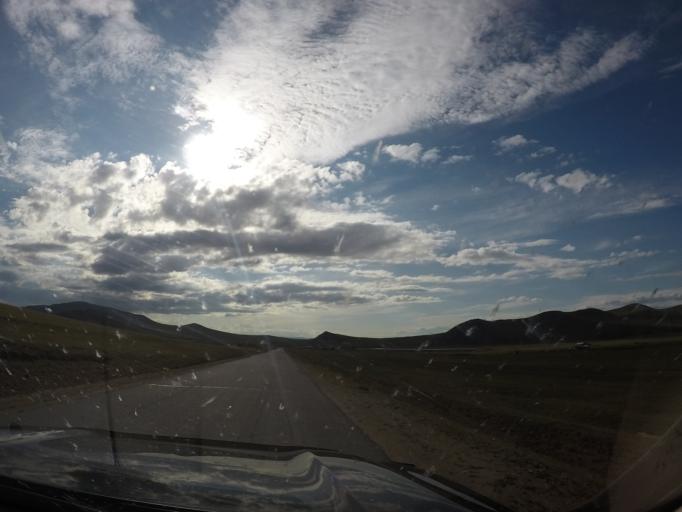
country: MN
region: Central Aimak
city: Bayandelger
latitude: 47.6932
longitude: 108.4853
